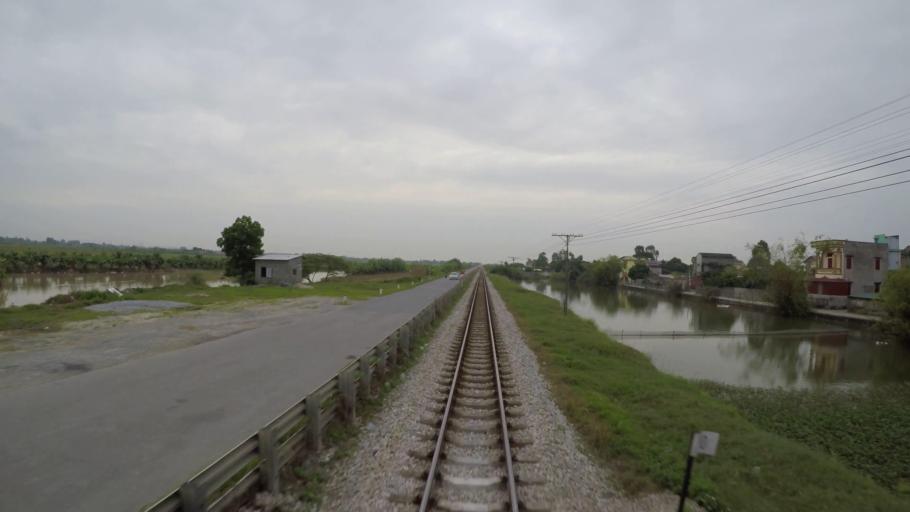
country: VN
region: Hung Yen
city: Ban Yen Nhan
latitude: 20.9802
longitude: 106.0807
